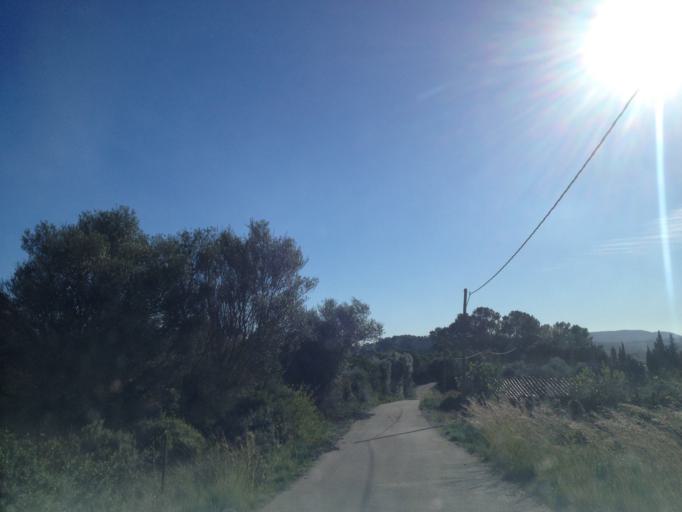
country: ES
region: Balearic Islands
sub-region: Illes Balears
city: Sineu
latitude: 39.6543
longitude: 3.0344
